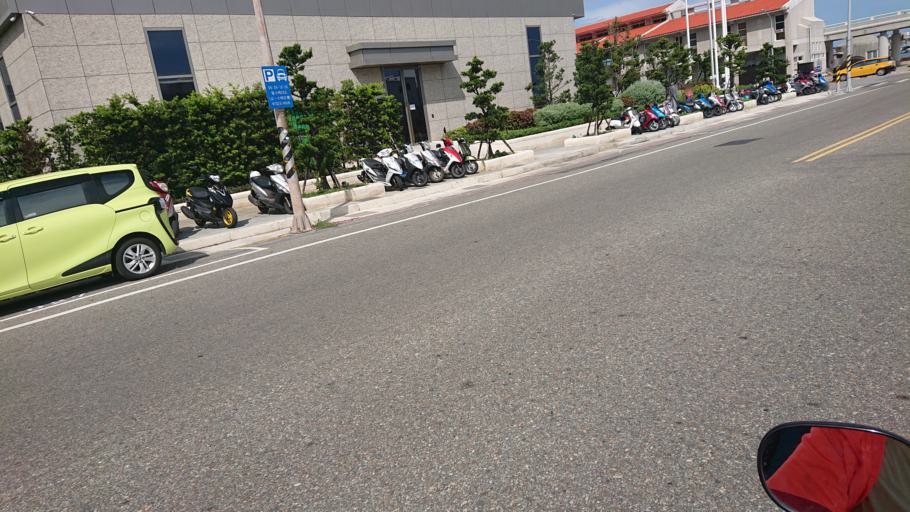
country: TW
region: Taiwan
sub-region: Penghu
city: Ma-kung
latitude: 23.5667
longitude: 119.5715
